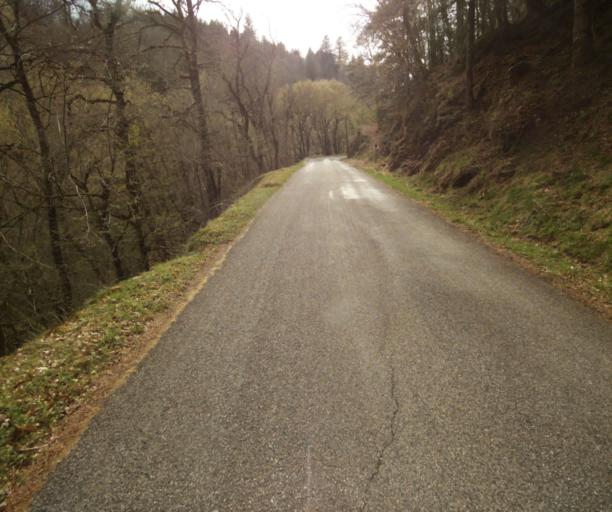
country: FR
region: Limousin
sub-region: Departement de la Correze
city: Argentat
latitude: 45.1922
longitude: 1.9816
